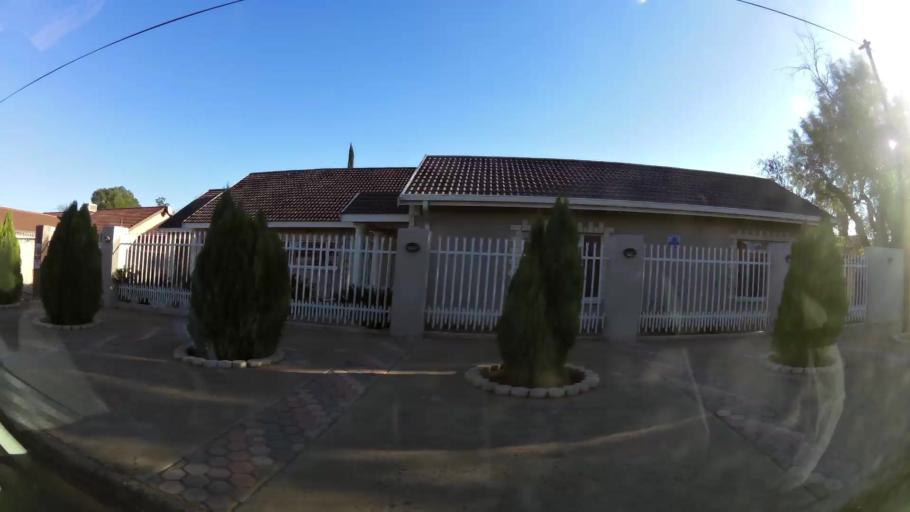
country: ZA
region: Northern Cape
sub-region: Frances Baard District Municipality
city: Kimberley
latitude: -28.7473
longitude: 24.7400
